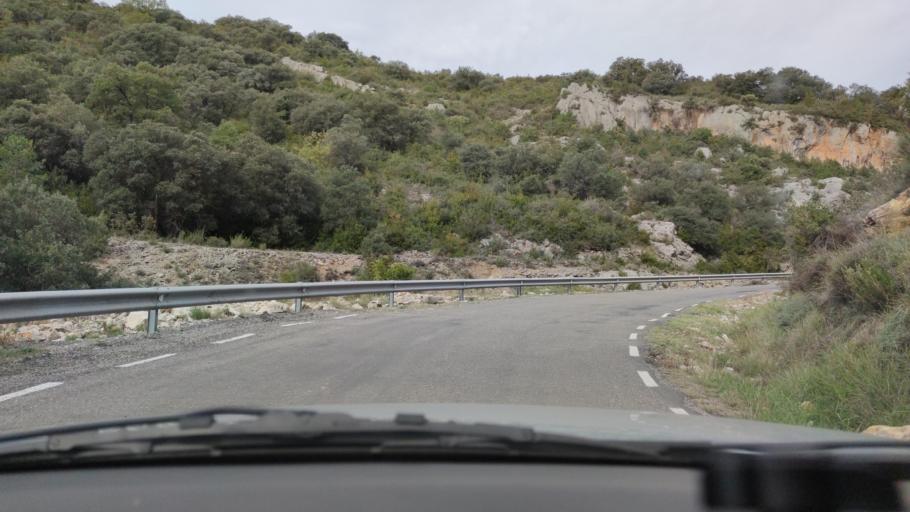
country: ES
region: Catalonia
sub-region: Provincia de Lleida
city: Artesa de Segre
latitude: 42.0098
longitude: 1.0323
